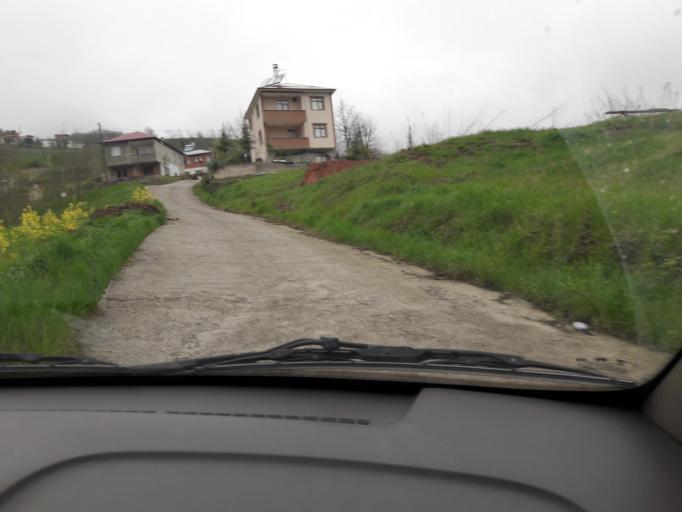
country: TR
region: Trabzon
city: Duzkoy
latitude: 40.9288
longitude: 39.4816
